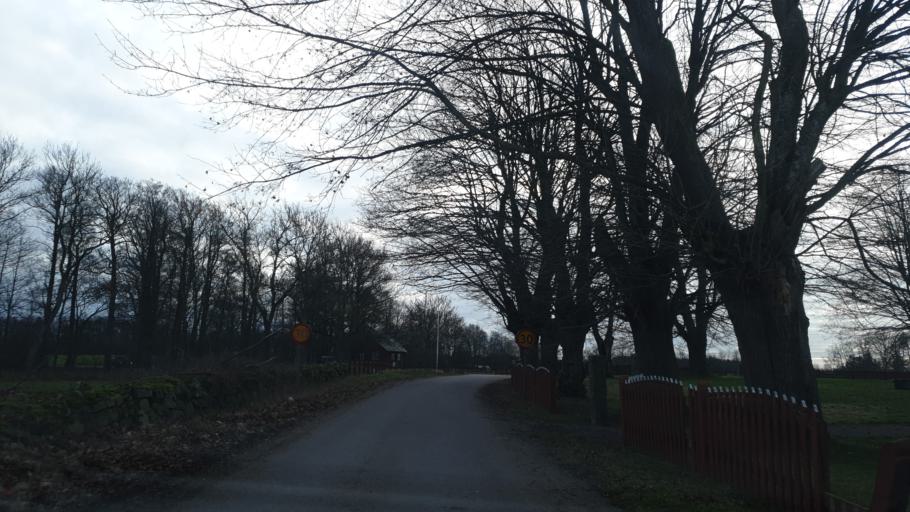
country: SE
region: Kalmar
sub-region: Torsas Kommun
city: Torsas
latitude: 56.3224
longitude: 16.0382
